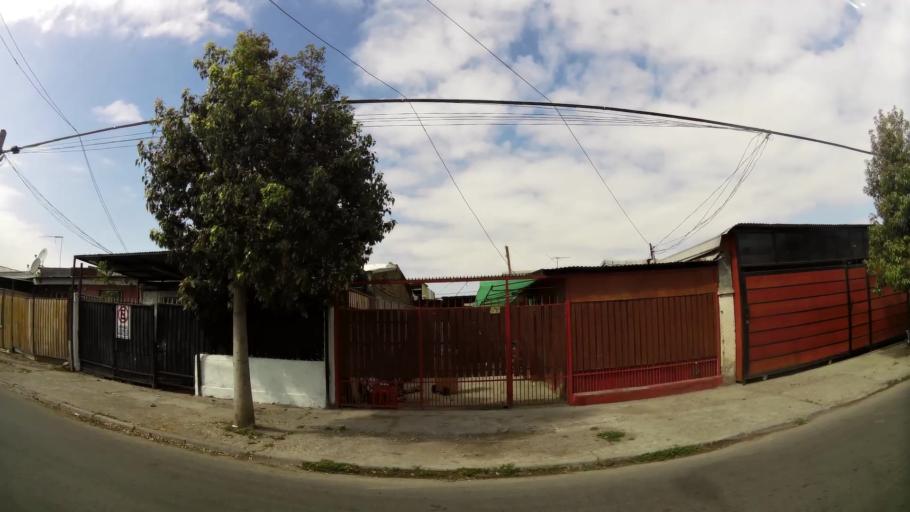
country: CL
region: Santiago Metropolitan
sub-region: Provincia de Santiago
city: Santiago
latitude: -33.5165
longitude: -70.6928
